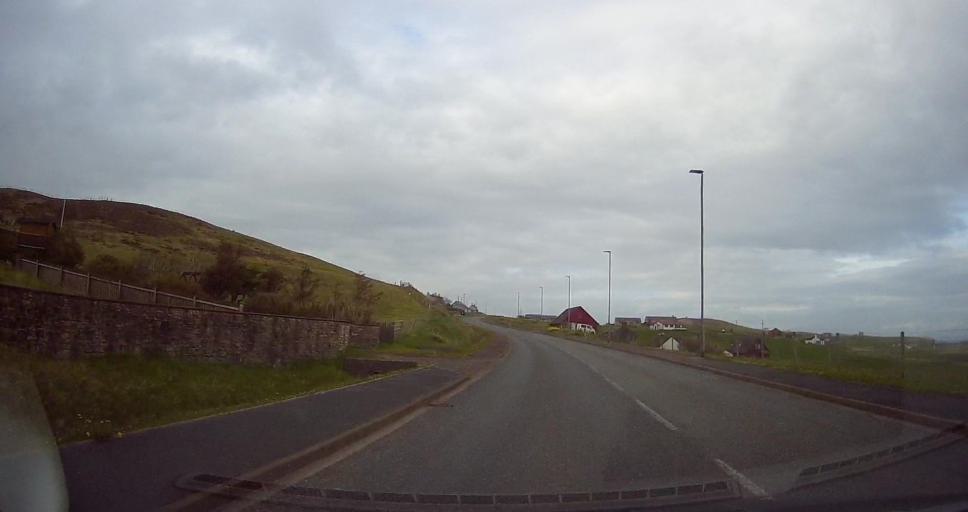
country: GB
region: Scotland
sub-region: Shetland Islands
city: Sandwick
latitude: 60.0413
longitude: -1.2299
